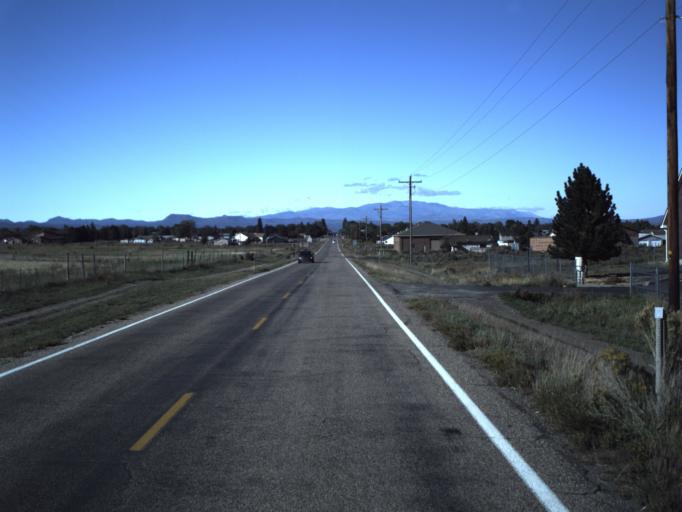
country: US
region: Utah
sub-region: Garfield County
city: Panguitch
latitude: 37.8077
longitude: -112.4354
